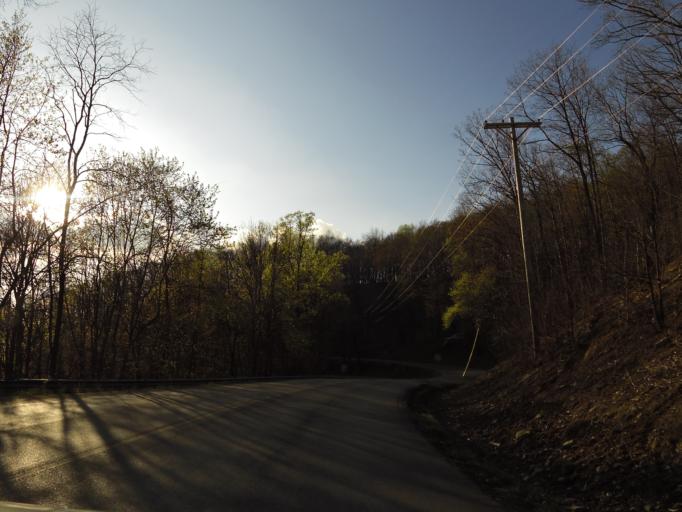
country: US
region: Kentucky
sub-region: Bell County
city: Middlesboro
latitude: 36.6297
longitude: -83.8557
